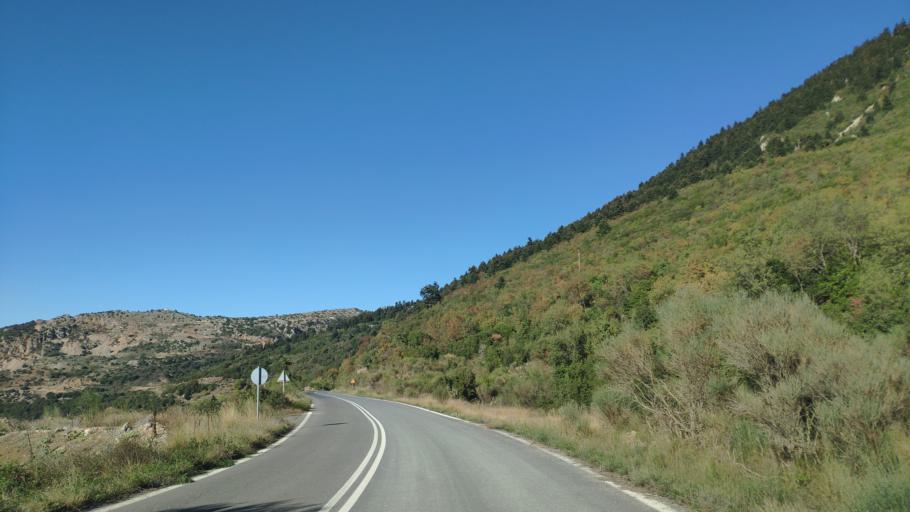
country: GR
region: Peloponnese
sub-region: Nomos Arkadias
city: Dimitsana
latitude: 37.5686
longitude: 22.0607
